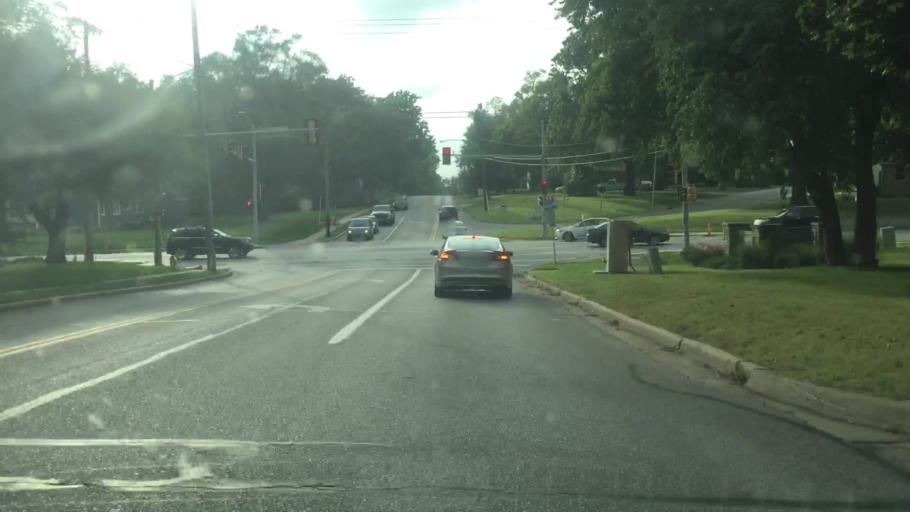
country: US
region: Kansas
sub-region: Johnson County
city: Shawnee
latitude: 39.0294
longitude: -94.7140
